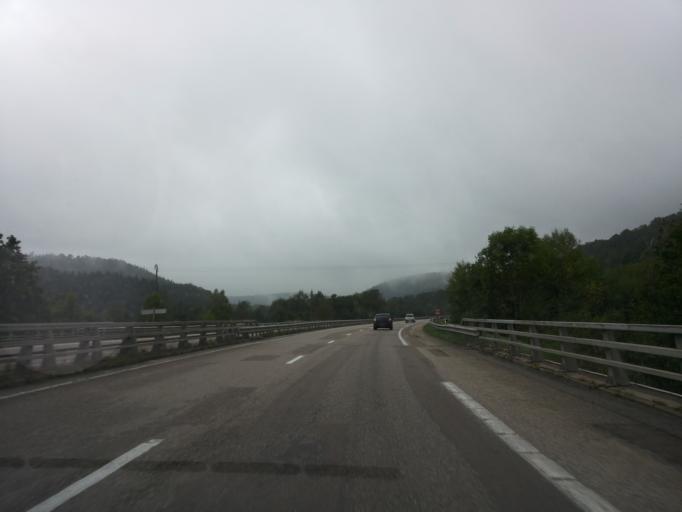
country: FR
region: Lorraine
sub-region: Departement des Vosges
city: Arches
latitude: 48.1272
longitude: 6.5161
